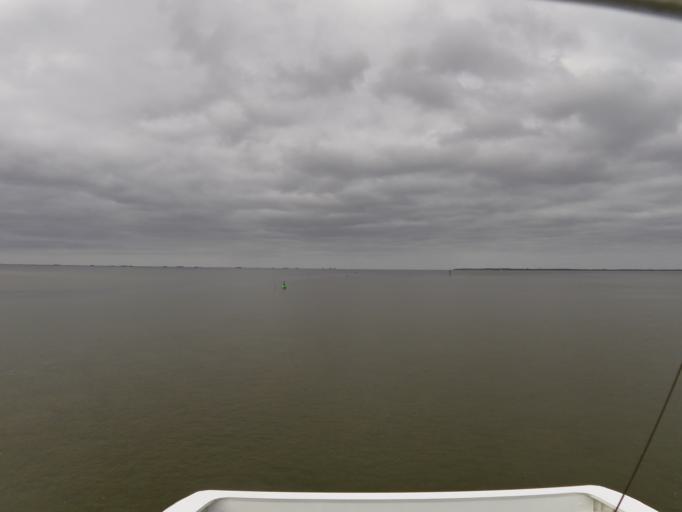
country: DE
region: Schleswig-Holstein
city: Dagebull
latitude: 54.7275
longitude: 8.6803
